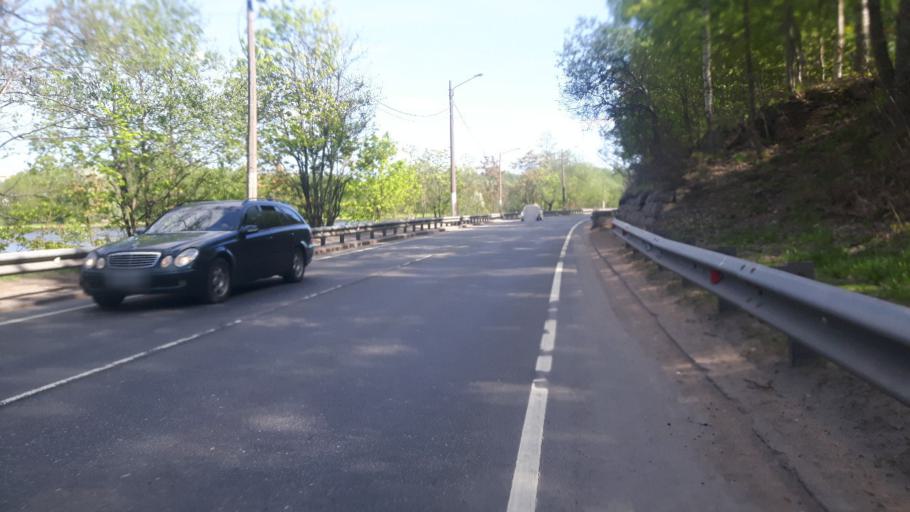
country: RU
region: Leningrad
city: Vyborg
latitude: 60.7241
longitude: 28.7106
